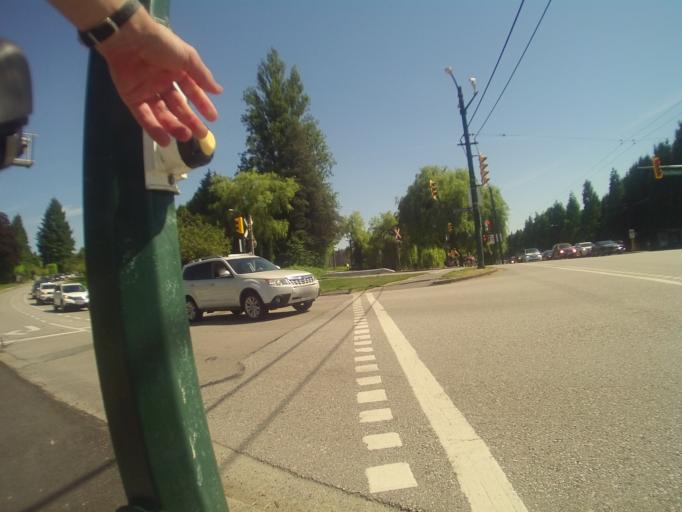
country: CA
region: British Columbia
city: Vancouver
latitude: 49.2517
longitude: -123.1530
